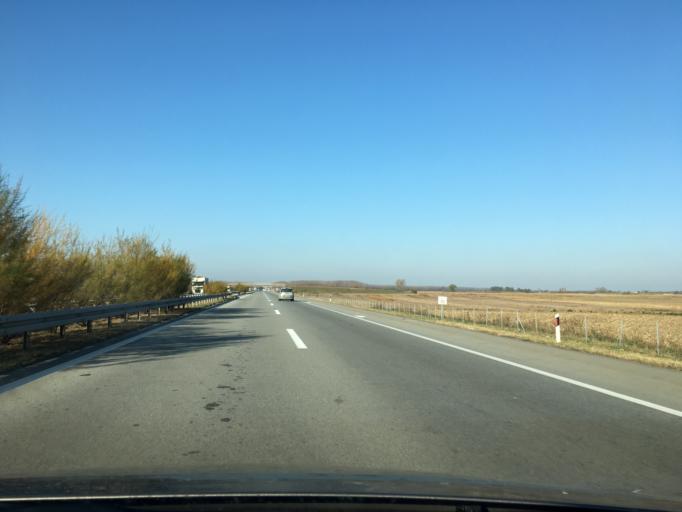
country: RS
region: Autonomna Pokrajina Vojvodina
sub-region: Juznobacki Okrug
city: Sremski Karlovci
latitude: 45.2708
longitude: 19.9460
